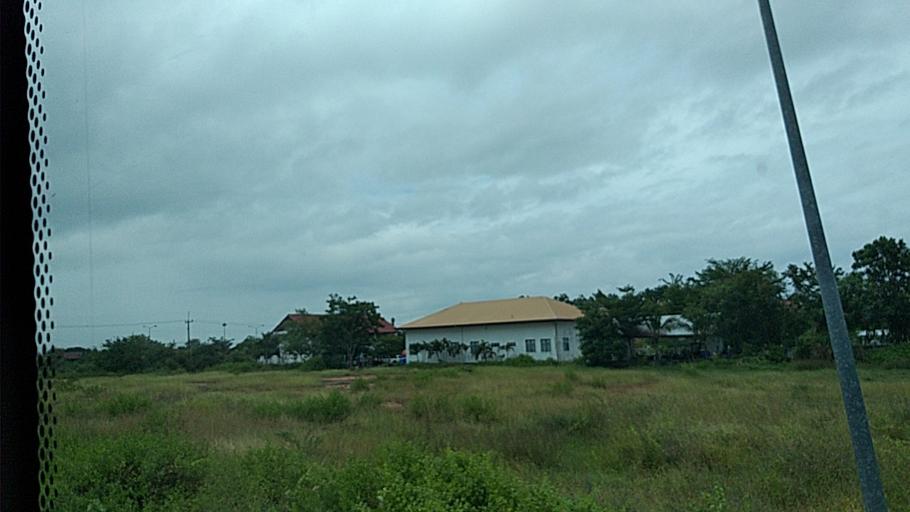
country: TH
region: Maha Sarakham
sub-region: Amphoe Borabue
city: Borabue
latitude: 16.0377
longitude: 103.1259
